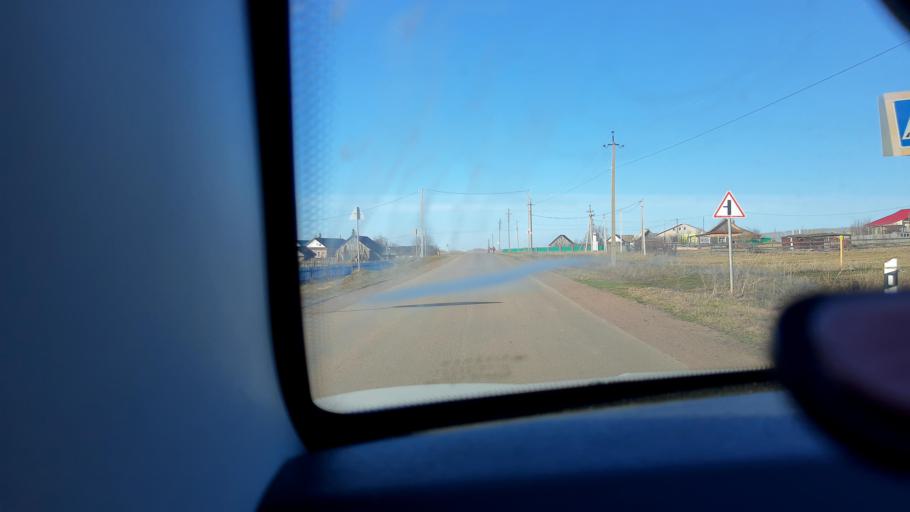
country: RU
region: Bashkortostan
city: Asanovo
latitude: 54.8420
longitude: 55.4582
